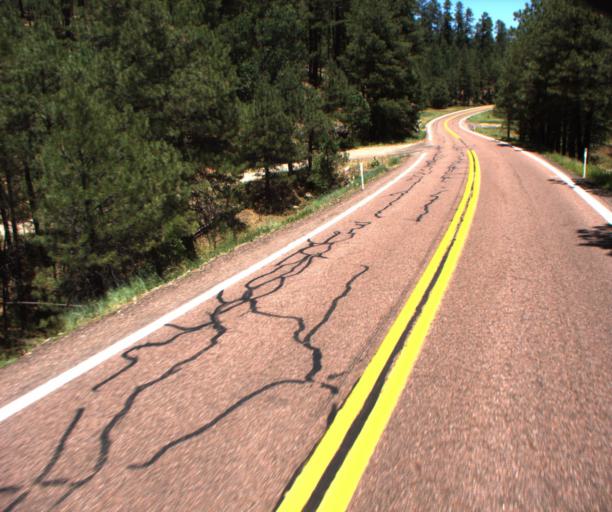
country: US
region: Arizona
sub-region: Gila County
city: Pine
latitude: 34.4961
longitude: -111.3689
